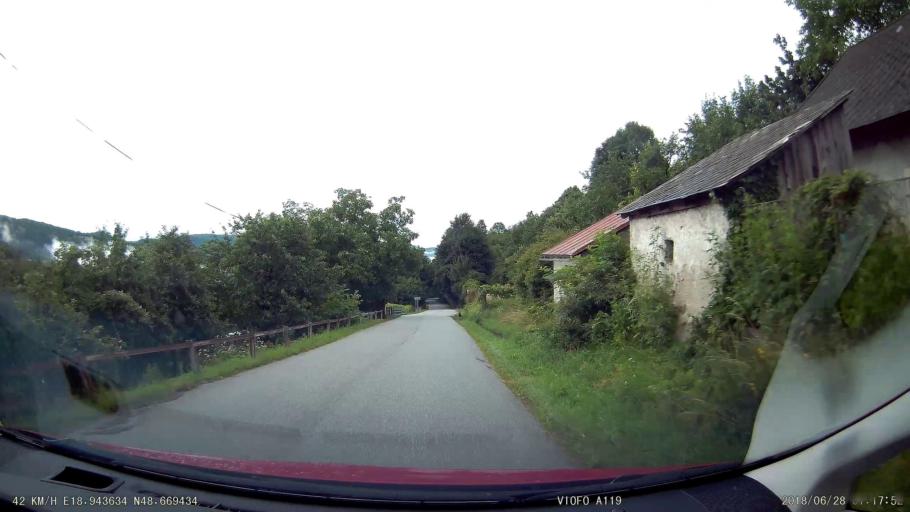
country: SK
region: Banskobystricky
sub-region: Okres Ziar nad Hronom
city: Kremnica
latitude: 48.6692
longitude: 18.9438
